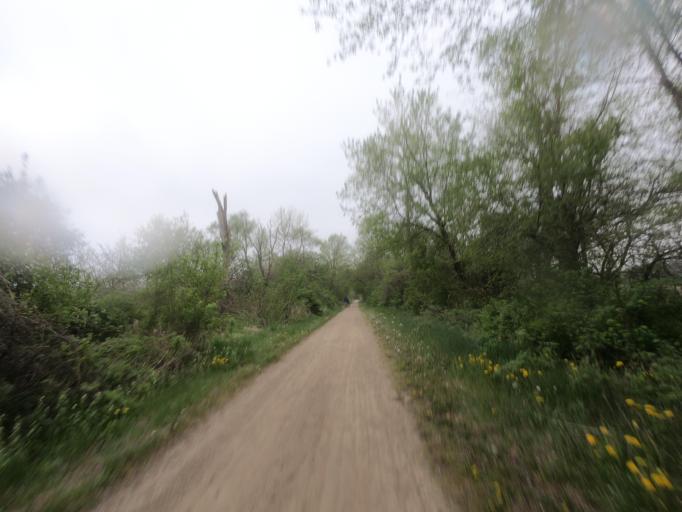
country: US
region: Wisconsin
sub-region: Jefferson County
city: Jefferson
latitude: 43.0367
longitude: -88.8191
